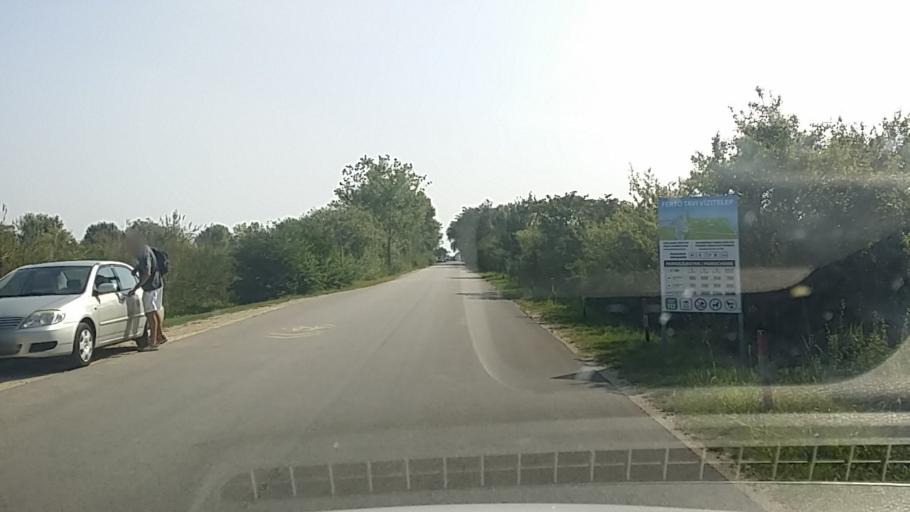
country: AT
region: Burgenland
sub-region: Eisenstadt-Umgebung
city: Morbisch am See
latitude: 47.7199
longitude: 16.6866
